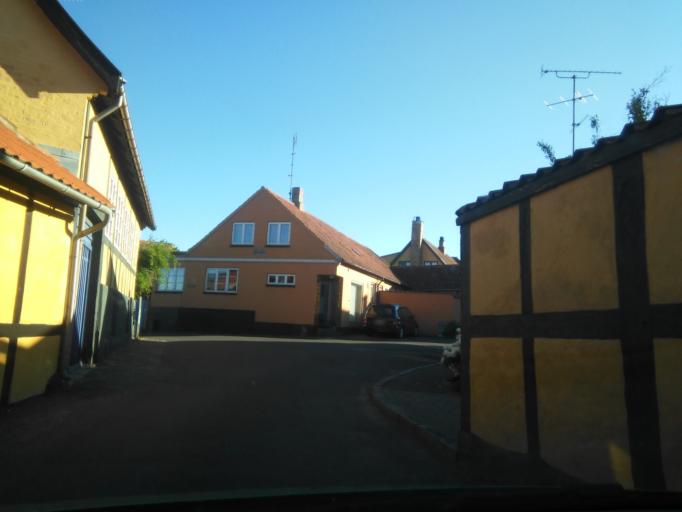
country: DK
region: Capital Region
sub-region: Bornholm Kommune
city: Ronne
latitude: 55.2755
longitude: 14.8044
